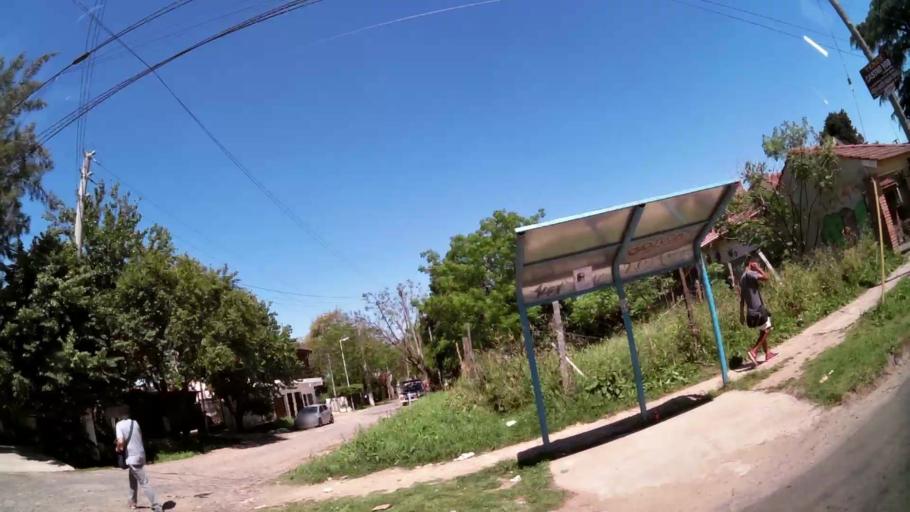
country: AR
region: Buenos Aires
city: Hurlingham
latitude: -34.4971
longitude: -58.6602
